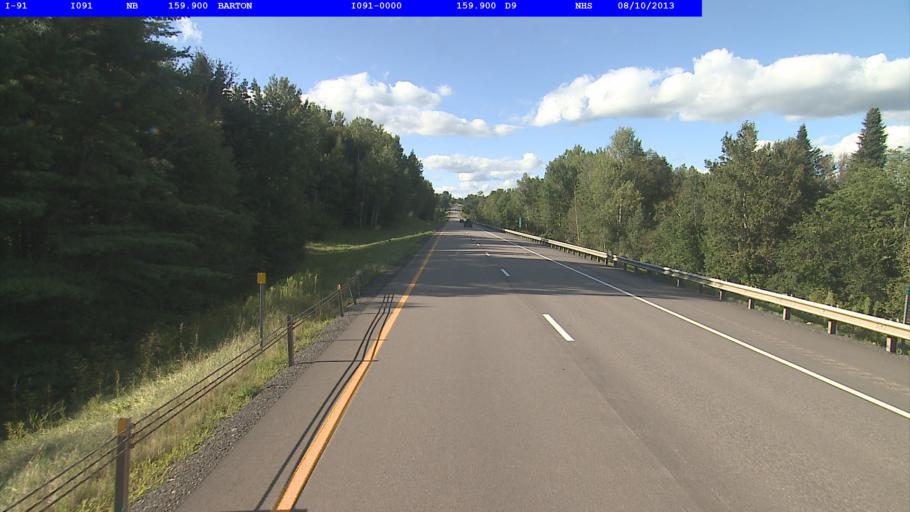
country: US
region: Vermont
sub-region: Orleans County
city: Newport
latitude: 44.7849
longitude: -72.2152
